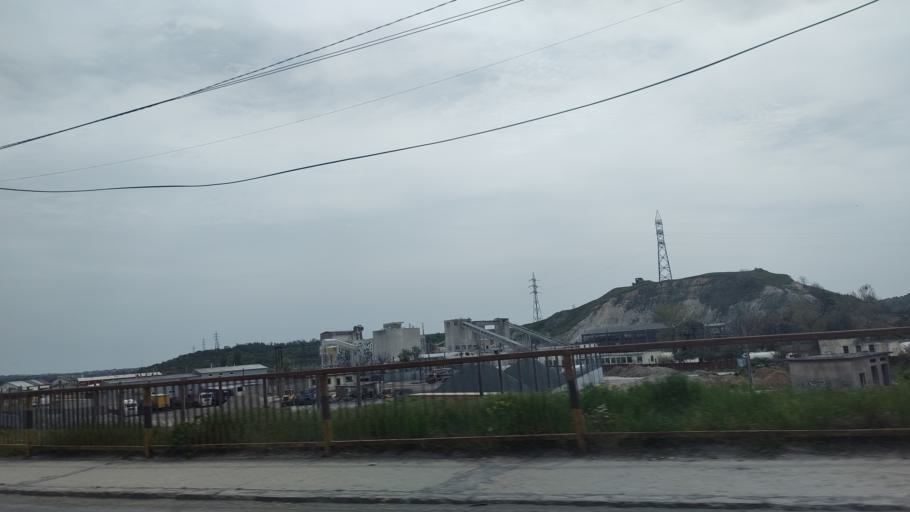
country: RO
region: Constanta
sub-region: Oras Murfatlar
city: Murfatlar
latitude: 44.1709
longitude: 28.4099
